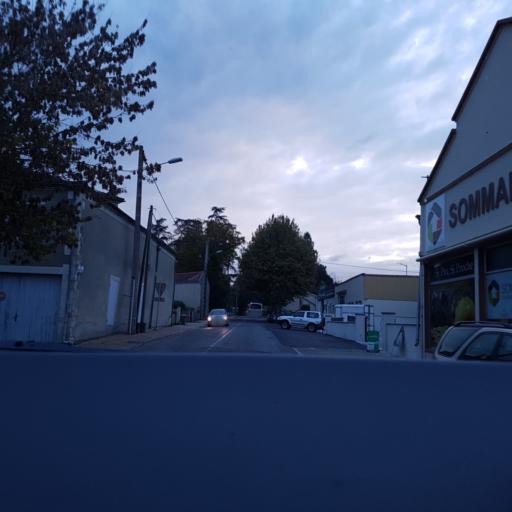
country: FR
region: Midi-Pyrenees
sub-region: Departement du Gers
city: Condom
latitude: 43.9548
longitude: 0.3640
